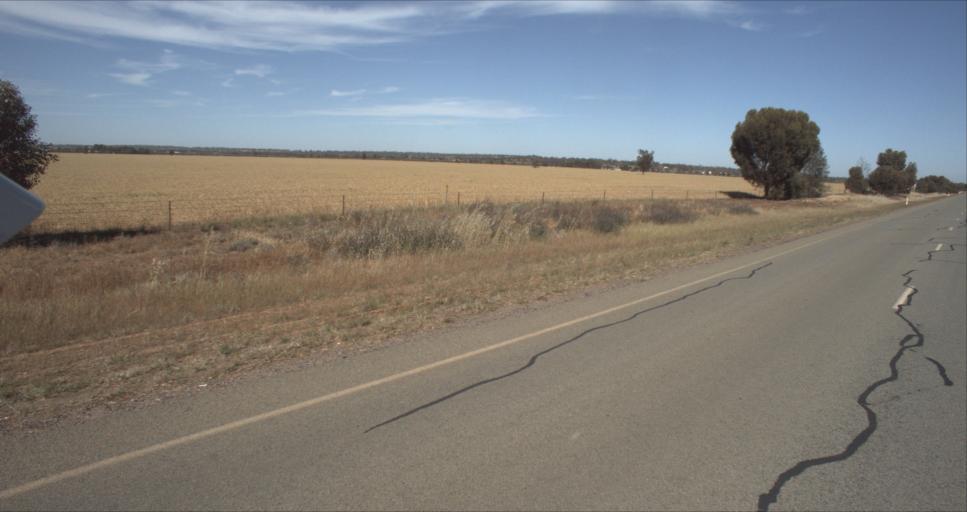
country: AU
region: New South Wales
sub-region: Leeton
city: Leeton
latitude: -34.5603
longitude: 146.4801
